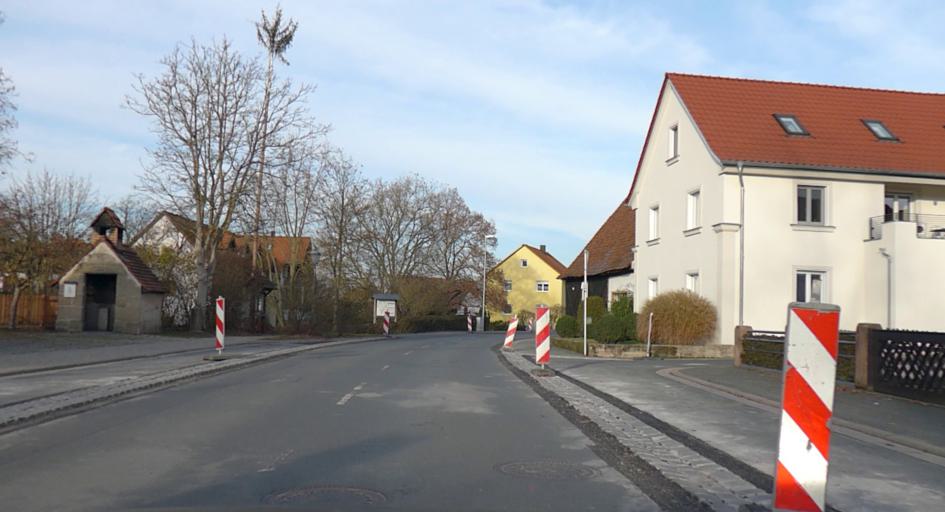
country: DE
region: Bavaria
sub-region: Regierungsbezirk Mittelfranken
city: Bubenreuth
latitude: 49.6315
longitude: 11.0382
